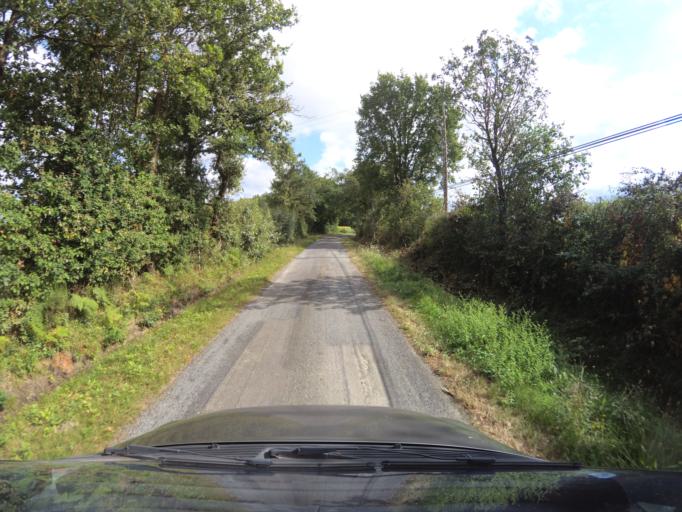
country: FR
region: Pays de la Loire
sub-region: Departement de la Vendee
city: Saint-Philbert-de-Bouaine
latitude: 46.9937
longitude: -1.4843
